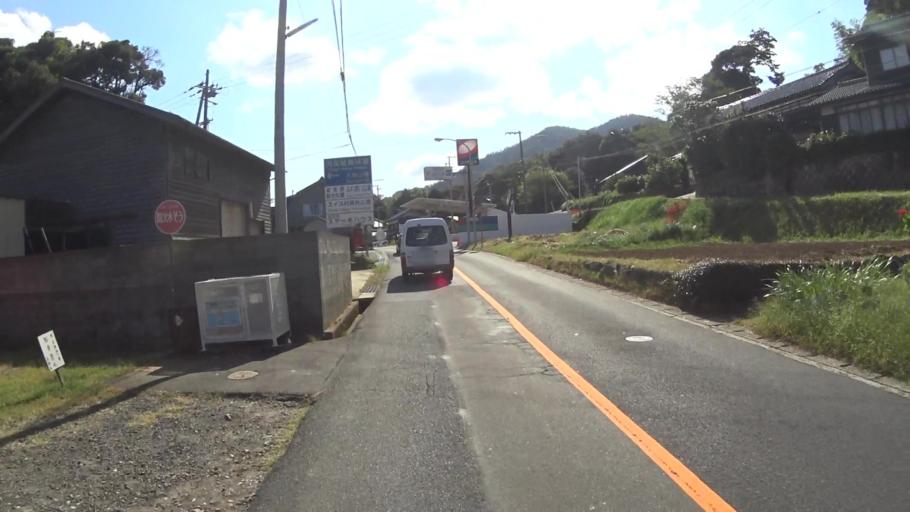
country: JP
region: Kyoto
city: Miyazu
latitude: 35.7516
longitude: 135.1679
